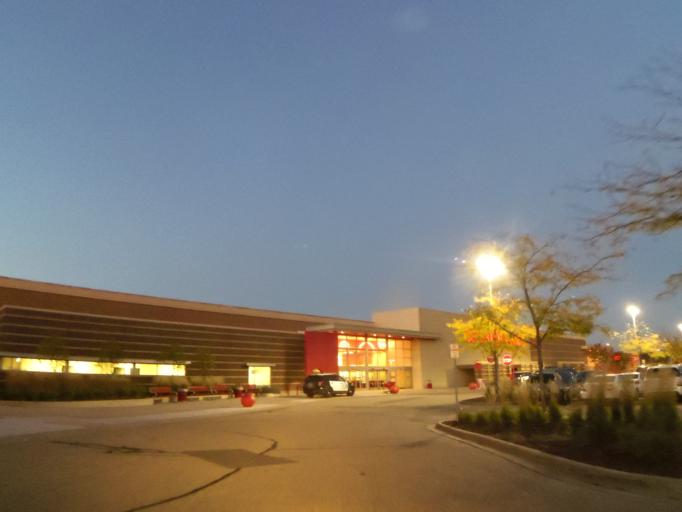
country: US
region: Minnesota
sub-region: Dakota County
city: Burnsville
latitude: 44.7485
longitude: -93.2904
